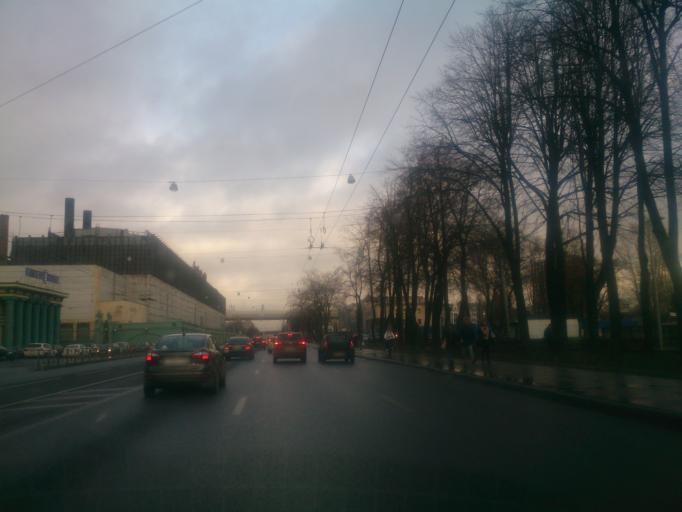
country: RU
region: St.-Petersburg
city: Avtovo
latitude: 59.8807
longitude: 30.2620
